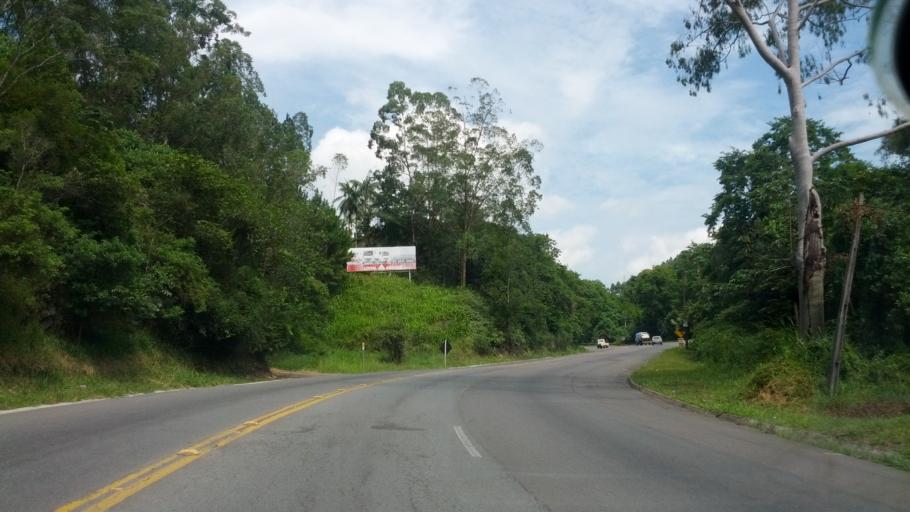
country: BR
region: Santa Catarina
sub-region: Ibirama
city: Ibirama
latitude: -27.0923
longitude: -49.5213
